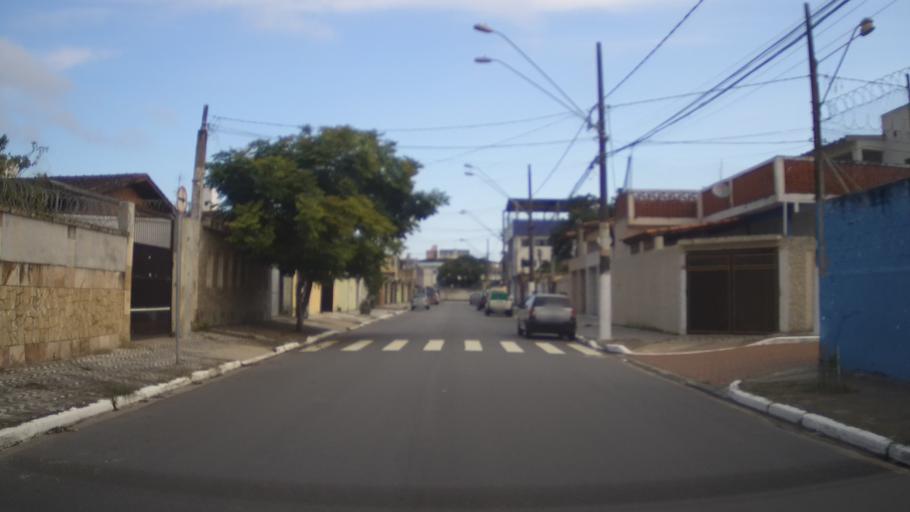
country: BR
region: Sao Paulo
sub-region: Praia Grande
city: Praia Grande
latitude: -24.0032
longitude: -46.4118
